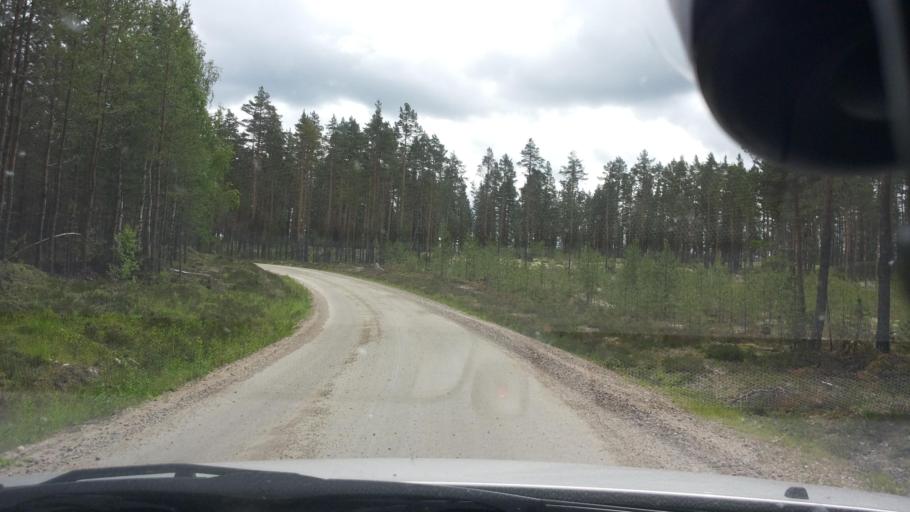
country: SE
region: Gaevleborg
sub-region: Ovanakers Kommun
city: Edsbyn
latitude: 61.5096
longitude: 15.3378
